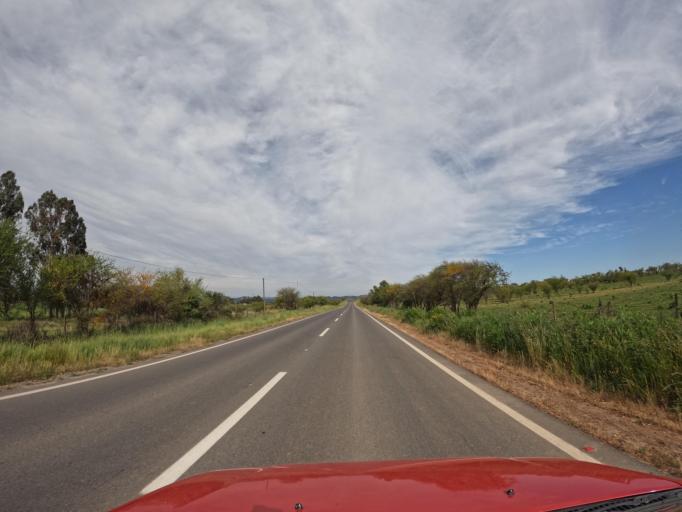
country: CL
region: Maule
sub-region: Provincia de Talca
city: Talca
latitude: -35.3720
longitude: -71.8420
